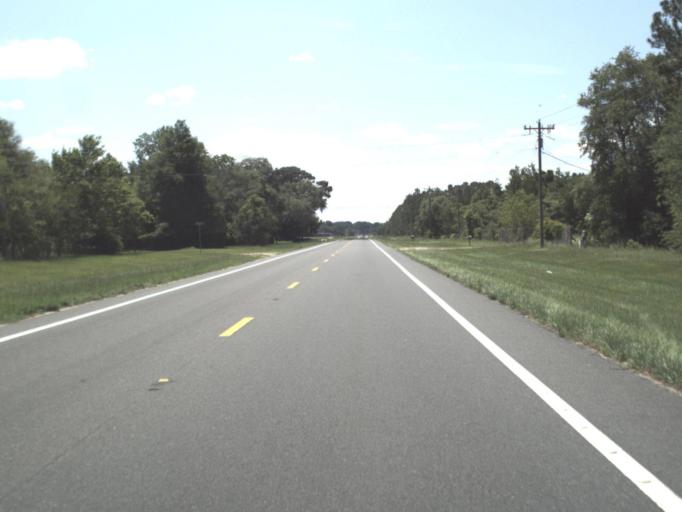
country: US
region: Florida
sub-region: Lafayette County
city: Mayo
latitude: 30.0780
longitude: -83.2124
